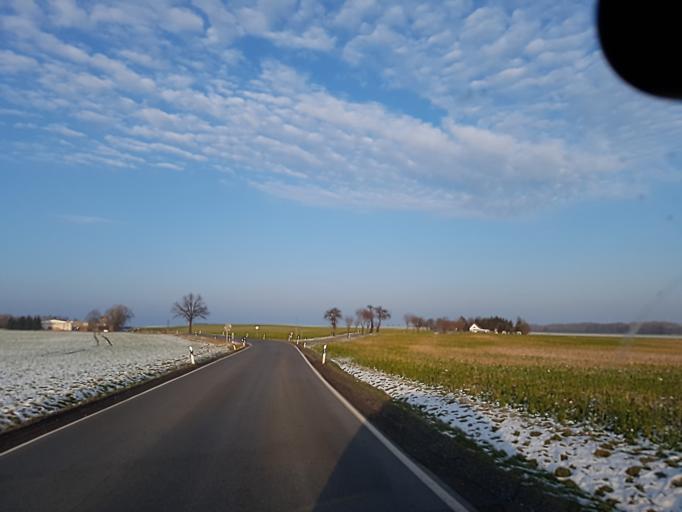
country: DE
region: Saxony
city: Naundorf
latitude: 51.2663
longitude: 13.1131
